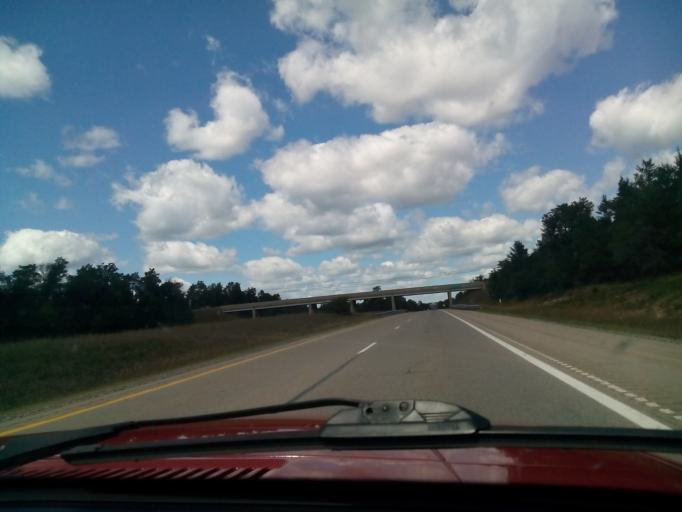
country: US
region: Michigan
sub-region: Crawford County
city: Grayling
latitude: 44.6693
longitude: -84.6961
